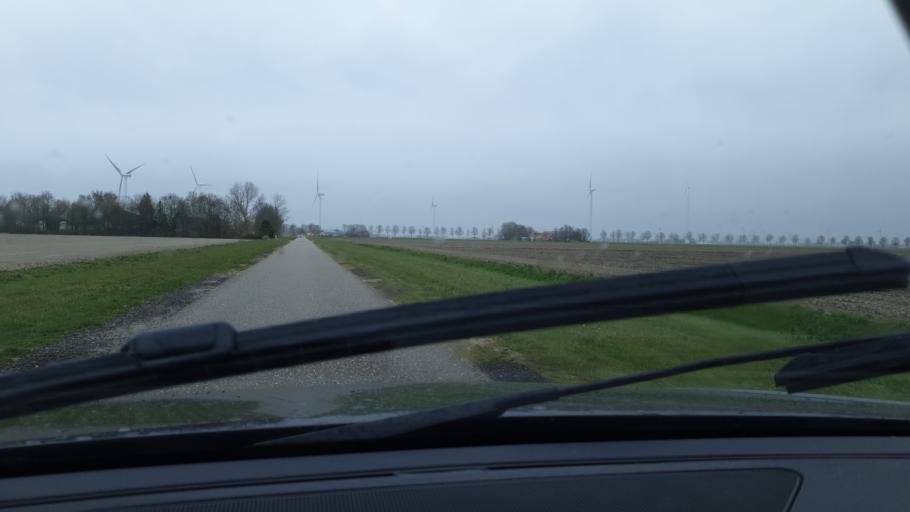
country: NL
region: Flevoland
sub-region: Gemeente Urk
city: Urk
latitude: 52.5632
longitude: 5.5754
